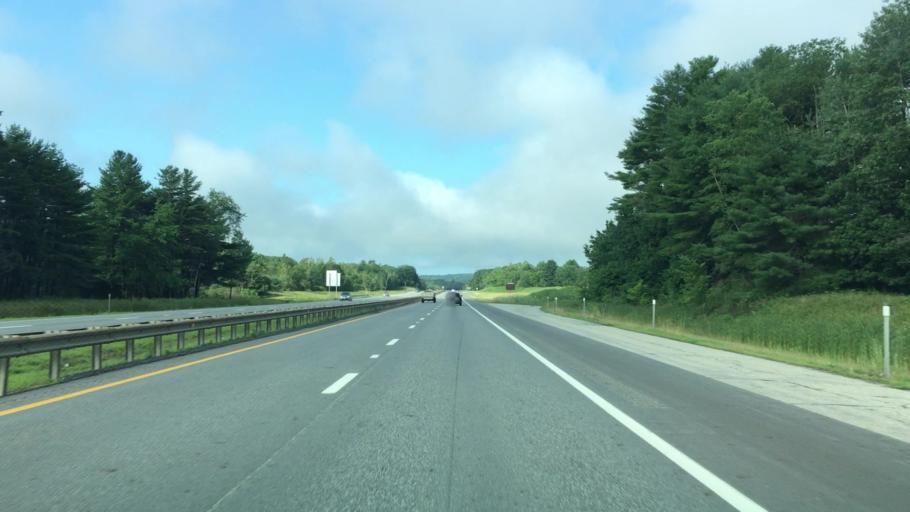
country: US
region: Maine
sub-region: Androscoggin County
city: Sabattus
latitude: 44.0772
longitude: -70.1252
